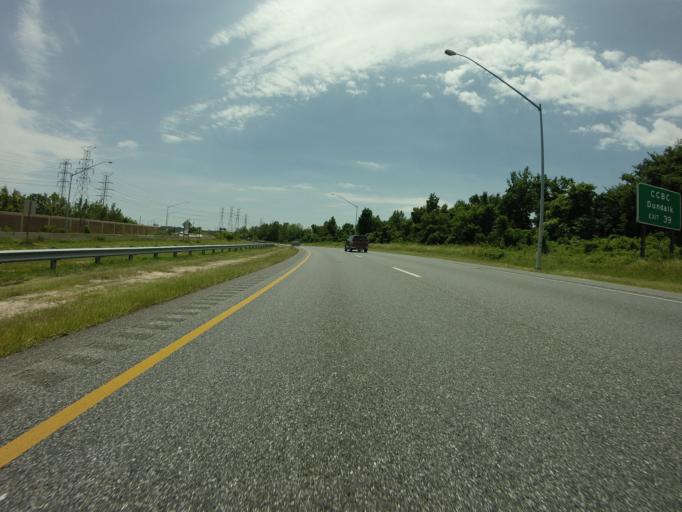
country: US
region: Maryland
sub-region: Baltimore County
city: Rosedale
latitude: 39.3119
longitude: -76.5027
